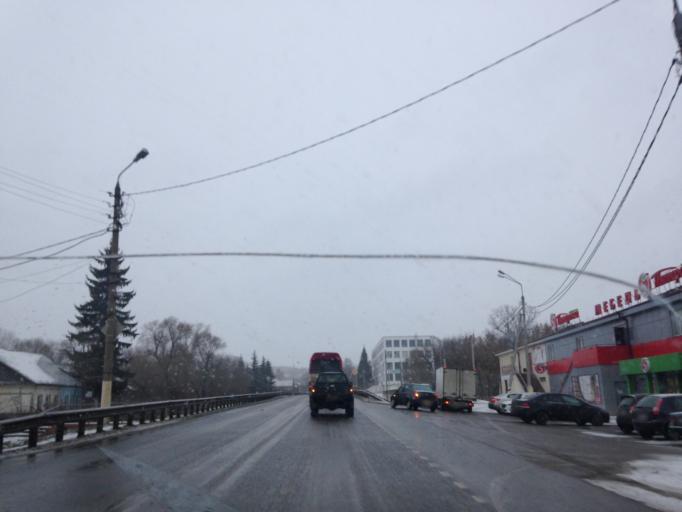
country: RU
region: Tula
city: Plavsk
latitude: 53.7104
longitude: 37.2953
